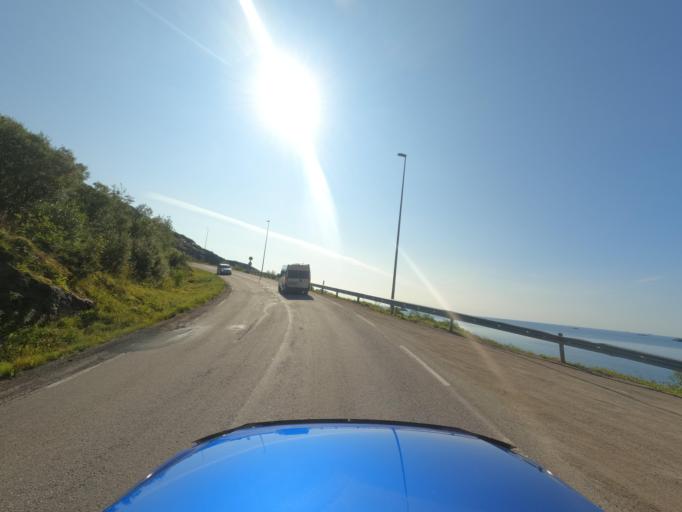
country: NO
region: Nordland
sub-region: Vagan
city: Svolvaer
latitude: 68.2443
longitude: 14.6331
